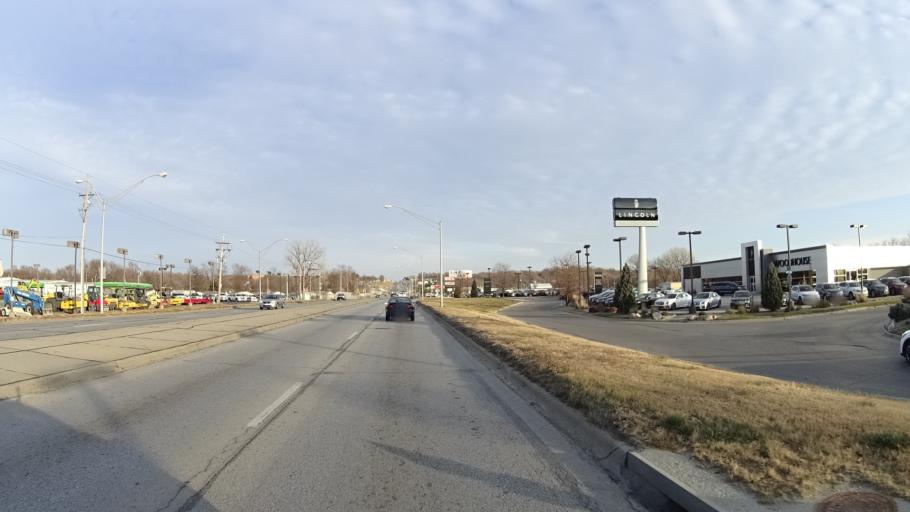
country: US
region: Nebraska
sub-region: Douglas County
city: Ralston
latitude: 41.2124
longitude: -96.0144
